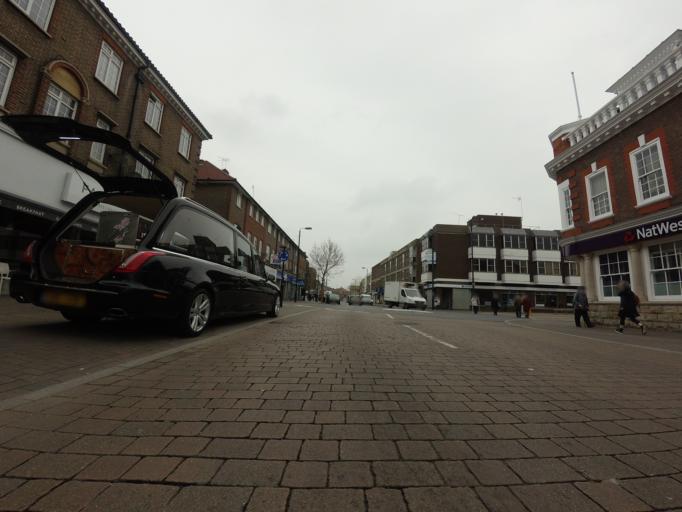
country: GB
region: England
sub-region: Greater London
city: Orpington
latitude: 51.3756
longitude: 0.0991
